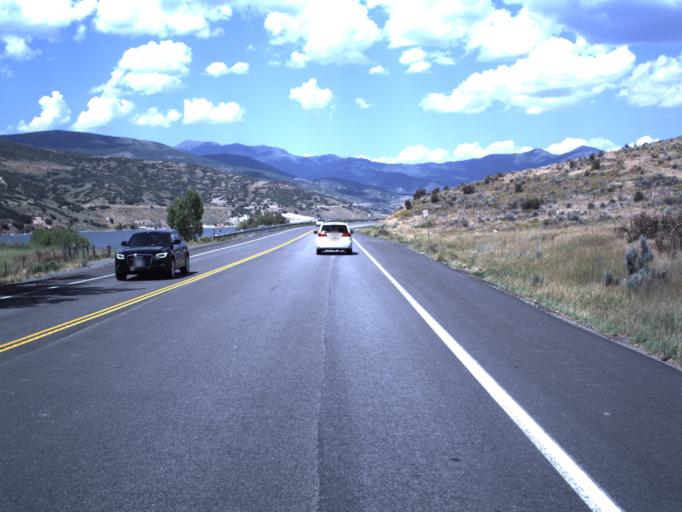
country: US
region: Utah
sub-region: Wasatch County
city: Midway
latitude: 40.4488
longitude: -111.4778
